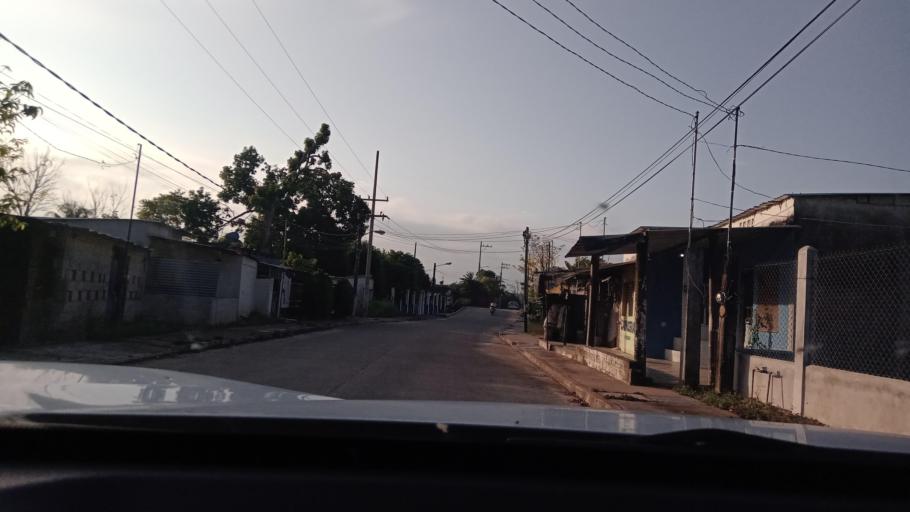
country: MX
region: Veracruz
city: Las Choapas
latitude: 17.8753
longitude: -94.0916
